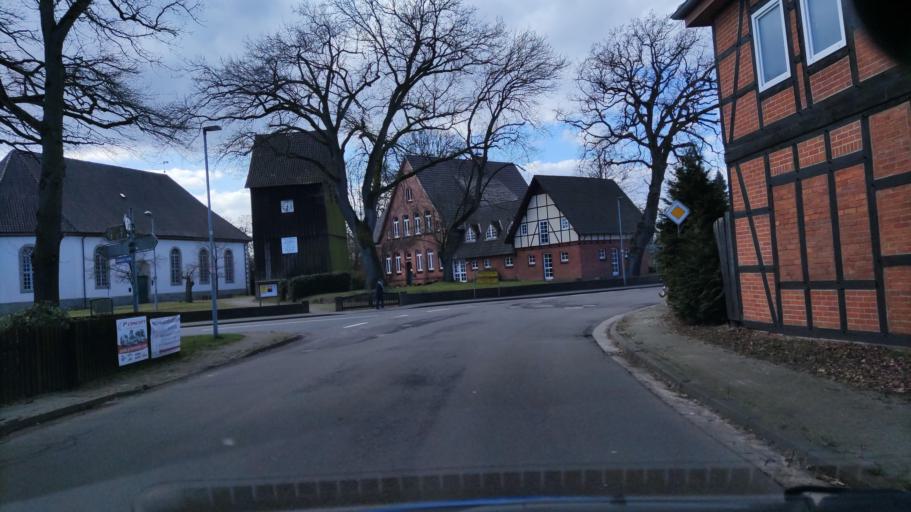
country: DE
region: Lower Saxony
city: Beedenbostel
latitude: 52.6442
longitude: 10.2581
